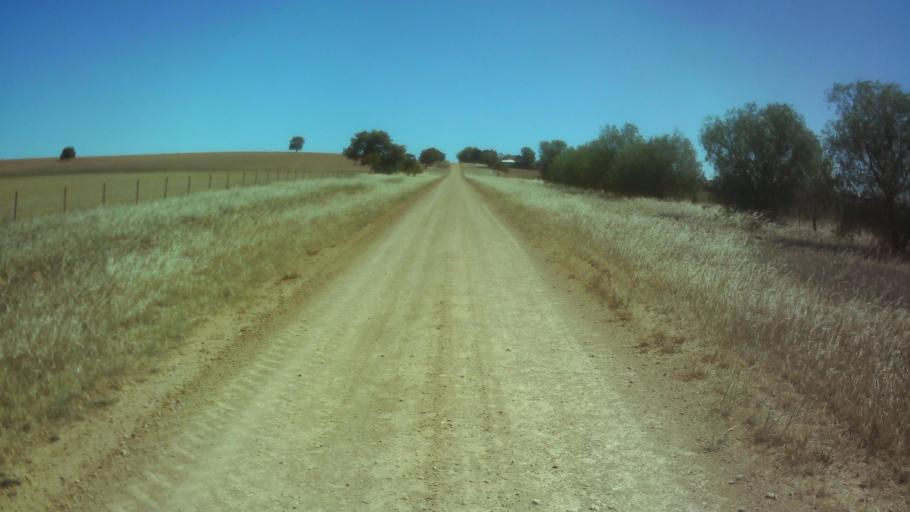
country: AU
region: New South Wales
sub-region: Weddin
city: Grenfell
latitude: -33.9900
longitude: 148.3575
